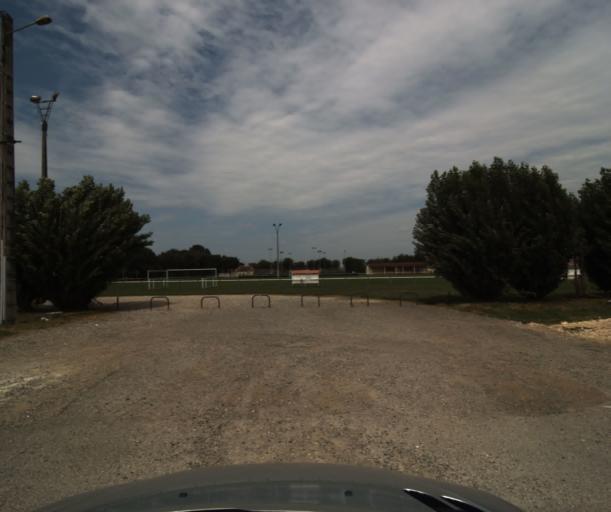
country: FR
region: Midi-Pyrenees
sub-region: Departement de la Haute-Garonne
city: Lacasse
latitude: 43.4229
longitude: 1.2814
